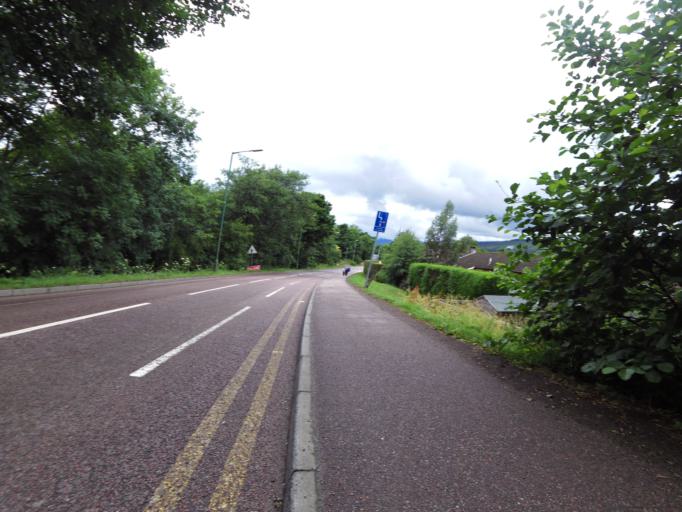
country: GB
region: Scotland
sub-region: Highland
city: Fort William
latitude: 56.8337
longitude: -5.0848
